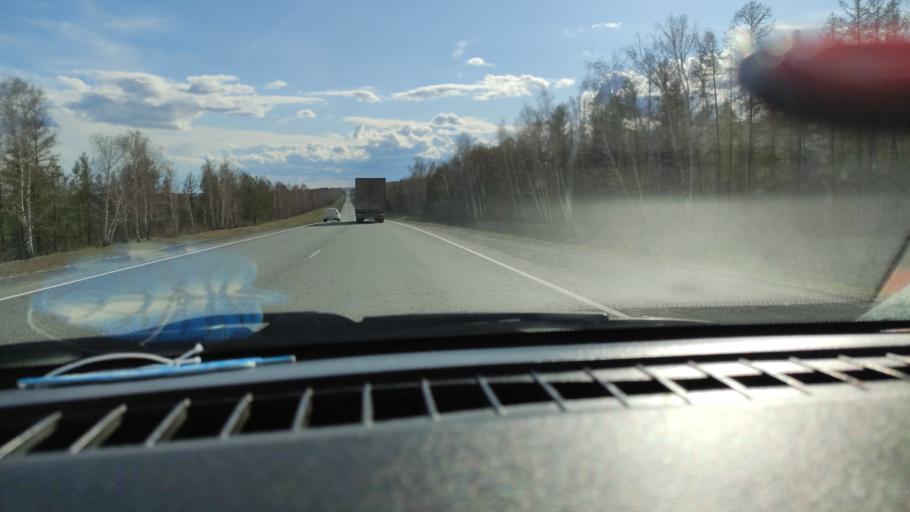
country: RU
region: Saratov
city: Sennoy
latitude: 52.1280
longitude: 46.8571
